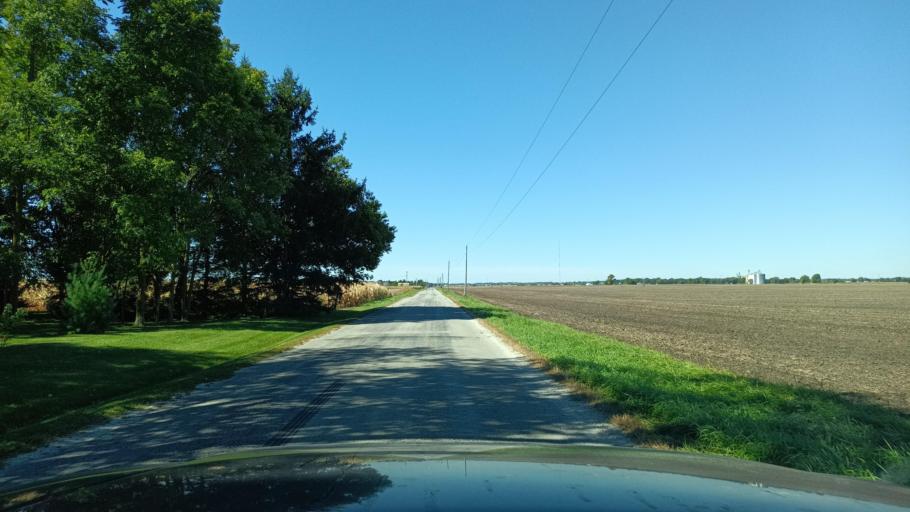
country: US
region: Illinois
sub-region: Champaign County
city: Mahomet
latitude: 40.0988
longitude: -88.3988
